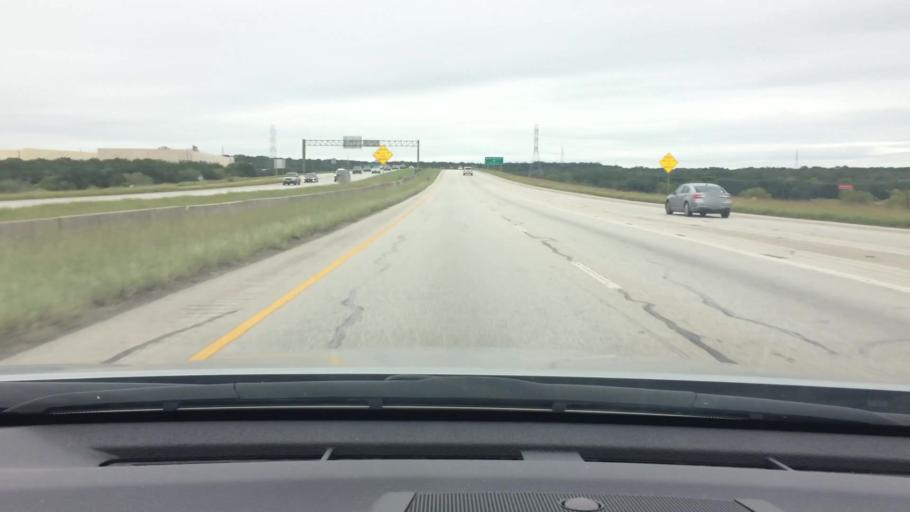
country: US
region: Texas
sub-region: Bexar County
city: Live Oak
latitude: 29.5968
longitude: -98.3552
